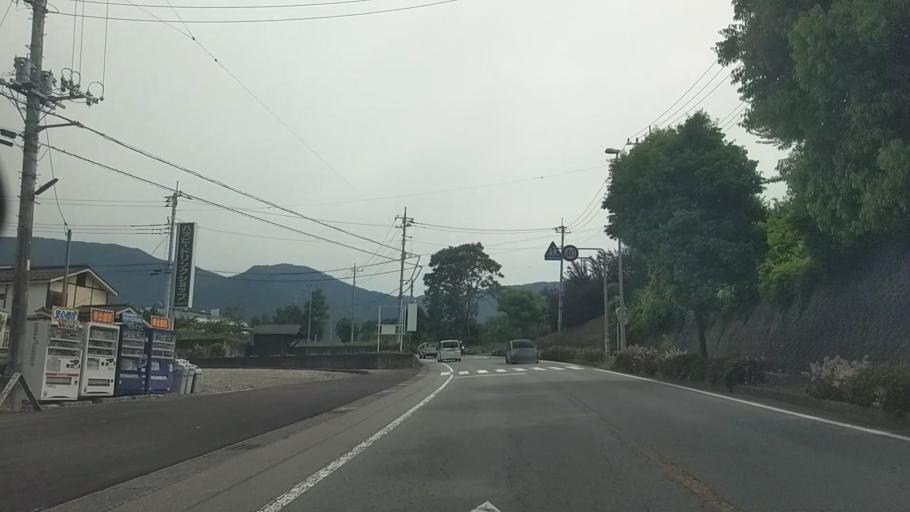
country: JP
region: Yamanashi
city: Isawa
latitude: 35.5867
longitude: 138.5901
